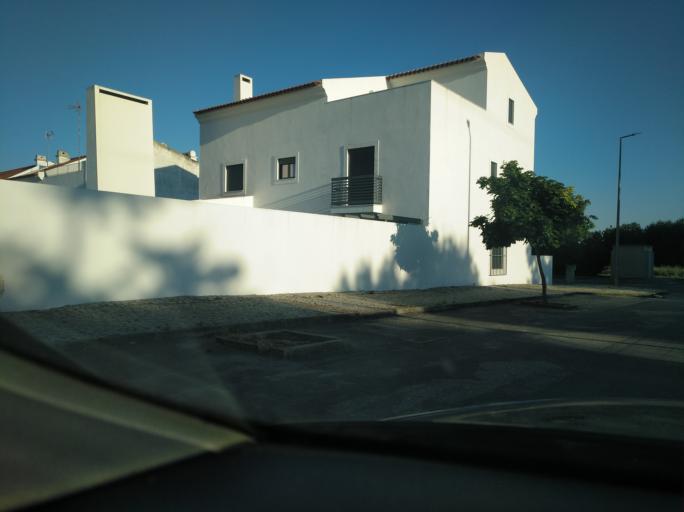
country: PT
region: Portalegre
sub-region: Elvas
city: Elvas
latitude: 38.8755
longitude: -7.1926
